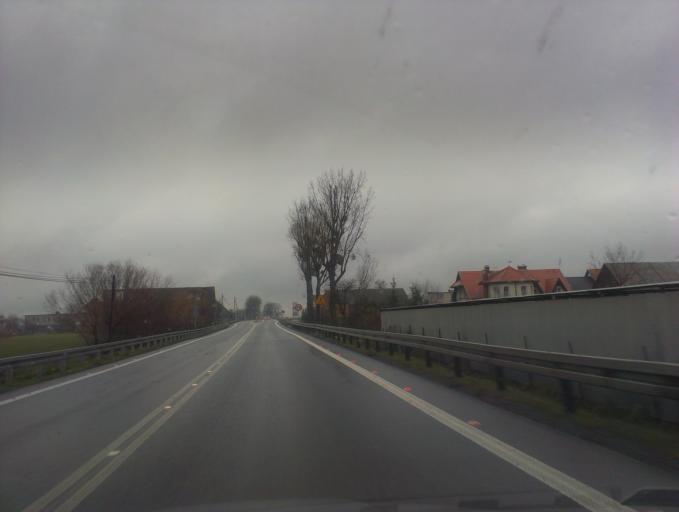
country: PL
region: Greater Poland Voivodeship
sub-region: Powiat obornicki
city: Oborniki
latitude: 52.5915
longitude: 16.8260
